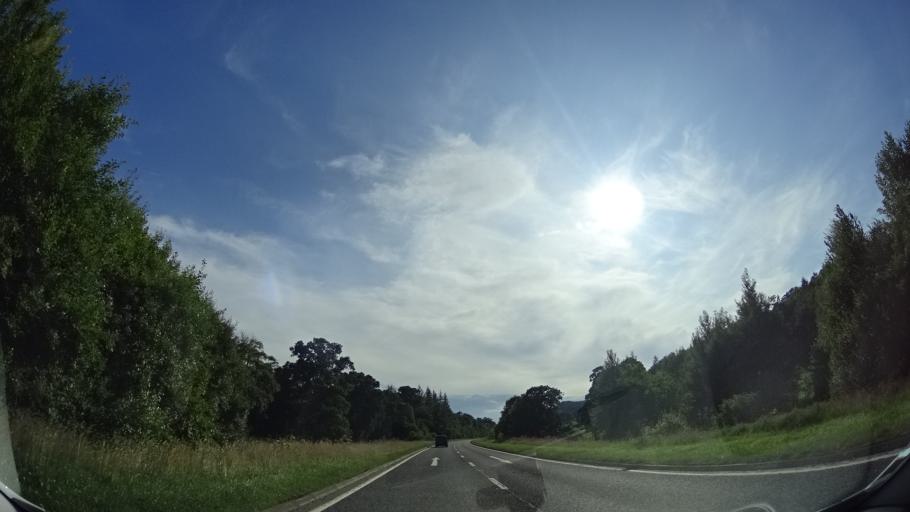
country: GB
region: Scotland
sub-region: Highland
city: Conon Bridge
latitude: 57.5737
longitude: -4.4528
